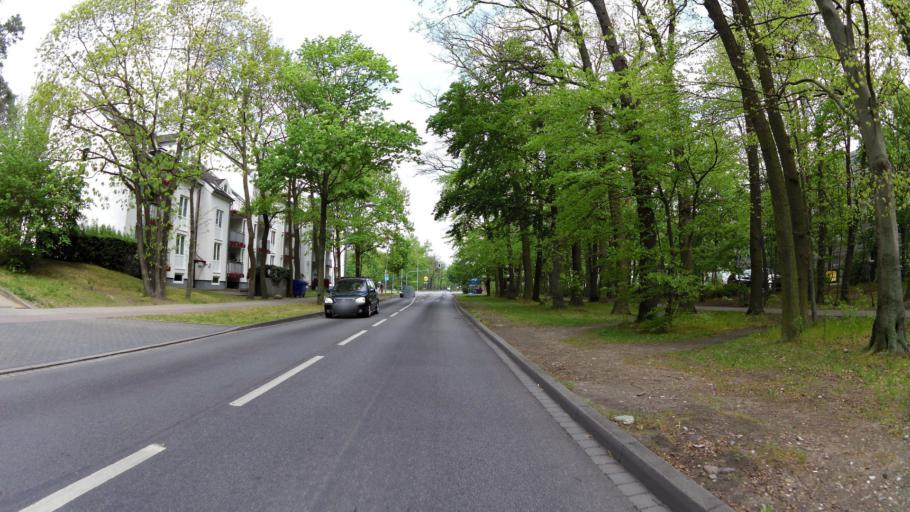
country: DE
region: Brandenburg
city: Konigs Wusterhausen
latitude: 52.2857
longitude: 13.6151
